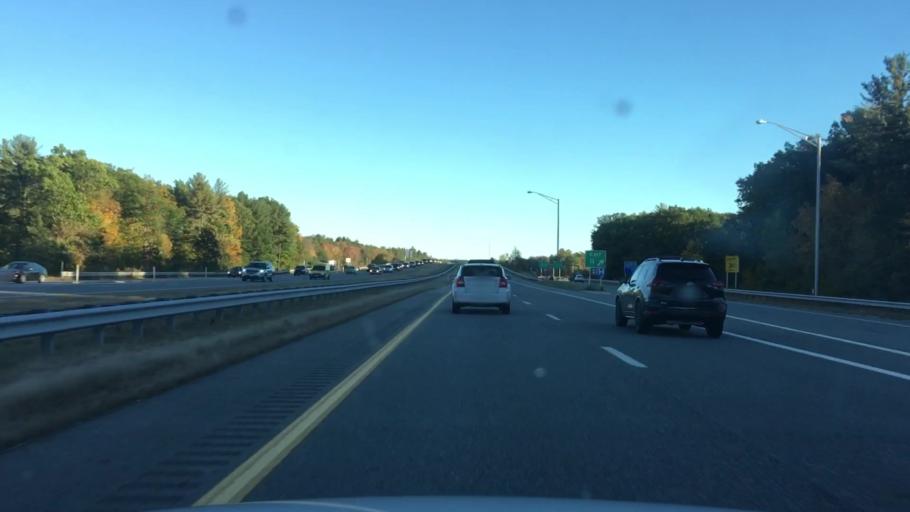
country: US
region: New Hampshire
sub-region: Rockingham County
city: Exeter
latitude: 42.9967
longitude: -70.9313
